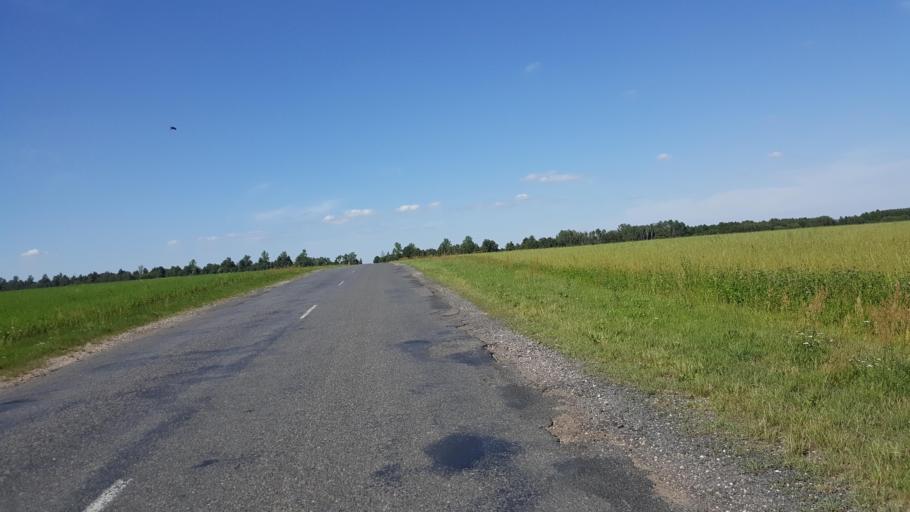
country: BY
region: Brest
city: Charnawchytsy
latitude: 52.3048
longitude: 23.6068
